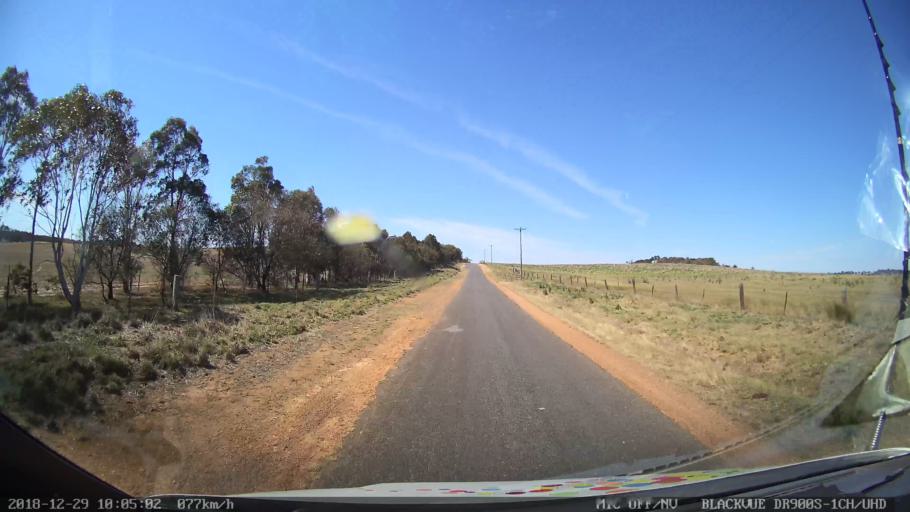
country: AU
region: New South Wales
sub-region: Goulburn Mulwaree
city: Goulburn
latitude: -34.8289
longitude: 149.4539
